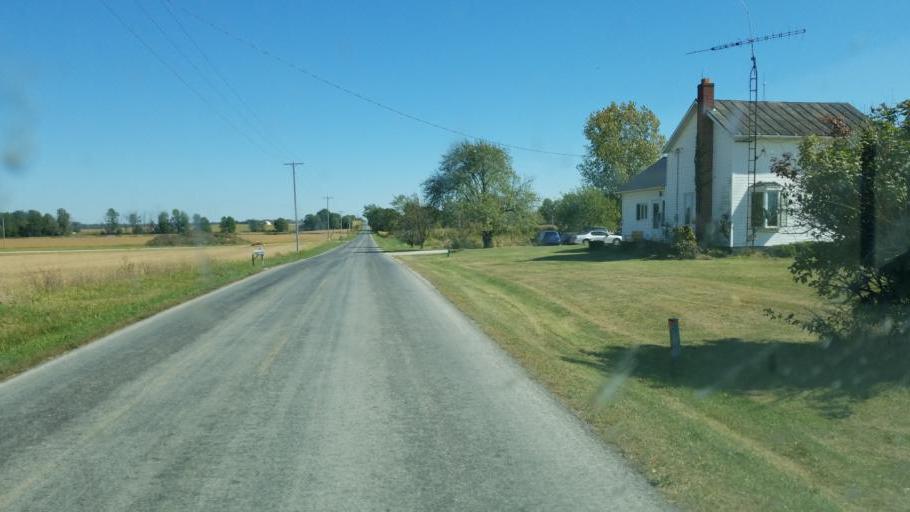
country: US
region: Ohio
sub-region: Huron County
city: Plymouth
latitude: 40.9943
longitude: -82.5966
